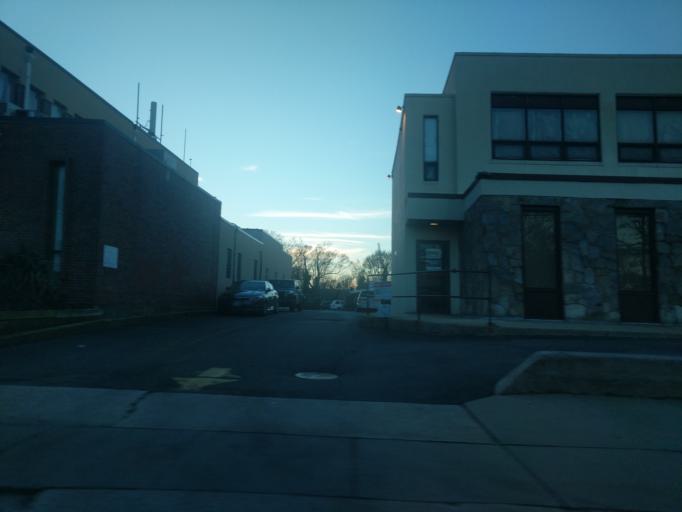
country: US
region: New York
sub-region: Nassau County
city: North Wantagh
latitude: 40.6928
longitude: -73.5079
